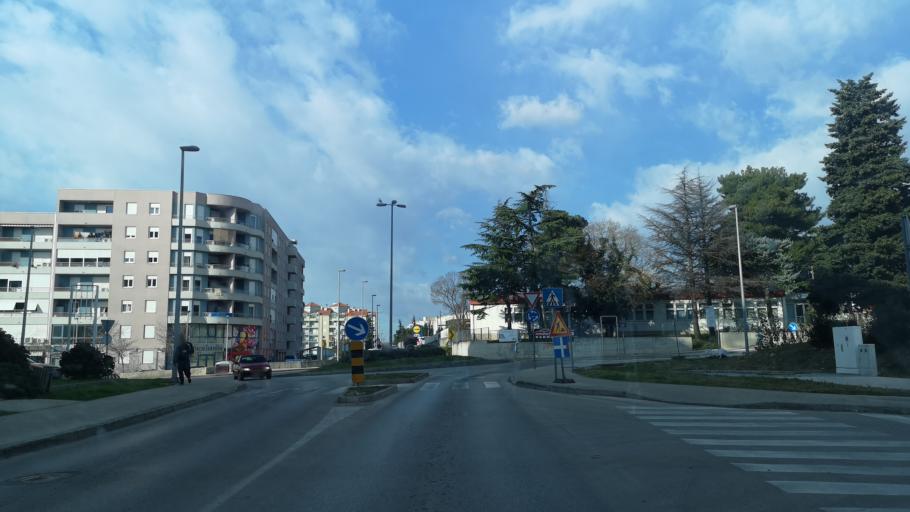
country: HR
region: Zadarska
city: Zadar
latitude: 44.1220
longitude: 15.2382
